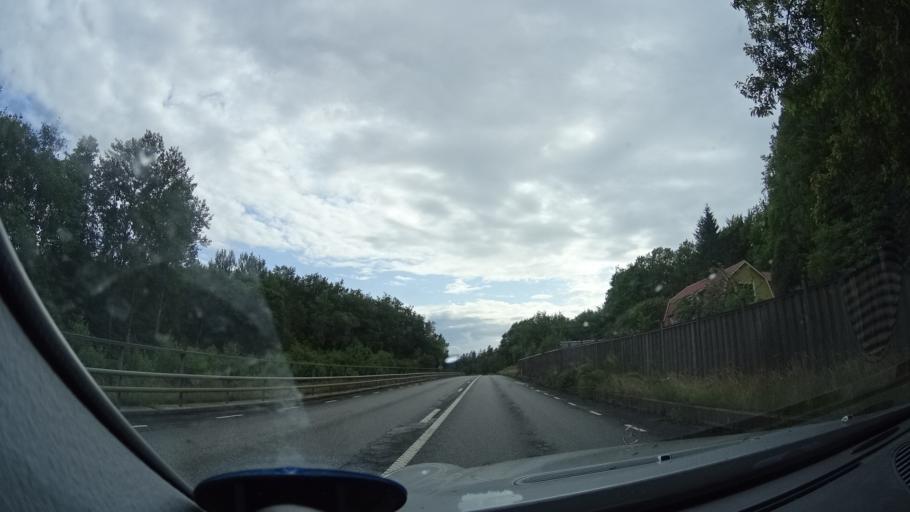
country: SE
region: Blekinge
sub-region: Karlshamns Kommun
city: Svangsta
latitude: 56.2603
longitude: 14.8387
